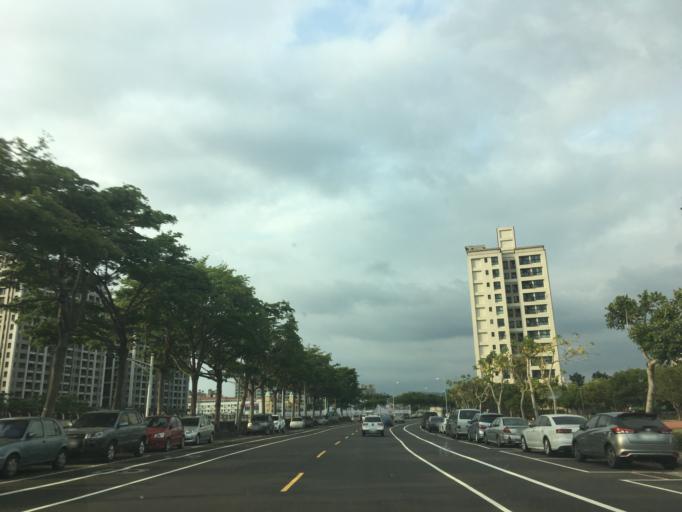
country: TW
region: Taiwan
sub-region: Taichung City
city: Taichung
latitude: 24.1506
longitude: 120.7012
